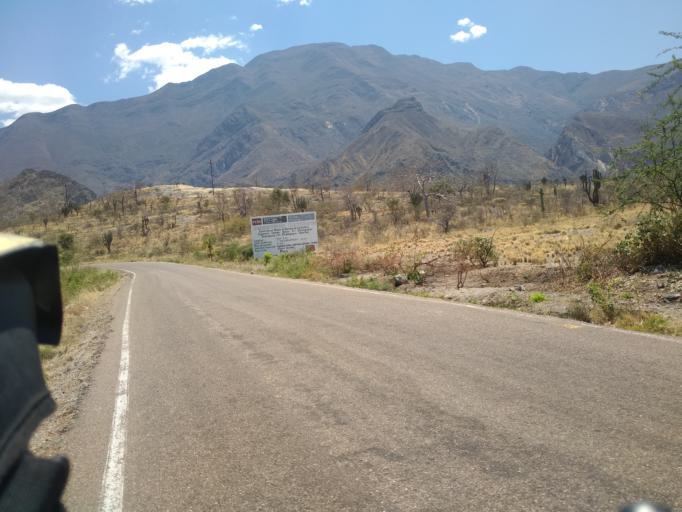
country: PE
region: Amazonas
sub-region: Provincia de Chachapoyas
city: Balsas
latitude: -6.8469
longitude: -78.0366
